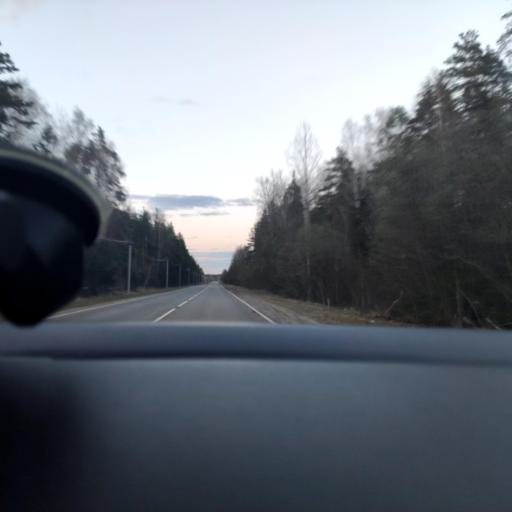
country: RU
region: Moskovskaya
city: Shaturtorf
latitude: 55.4505
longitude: 39.4406
